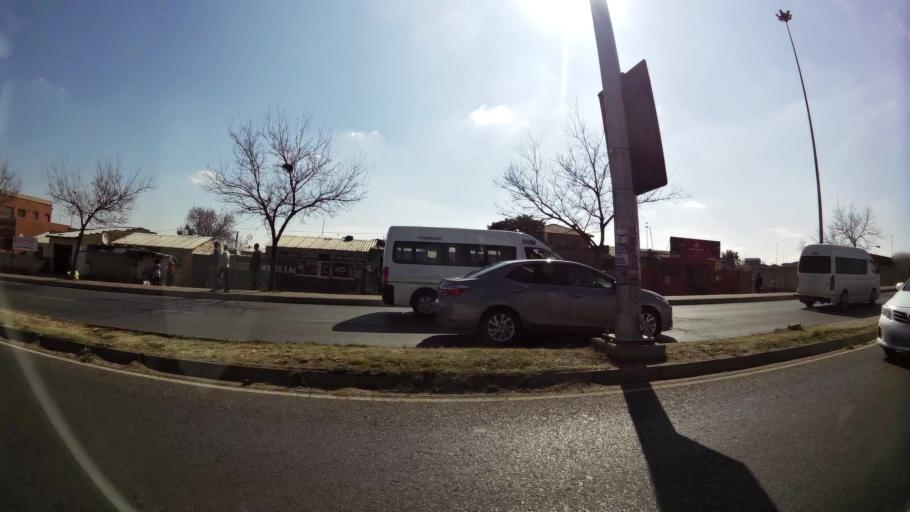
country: ZA
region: Gauteng
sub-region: City of Johannesburg Metropolitan Municipality
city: Soweto
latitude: -26.2823
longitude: 27.8579
